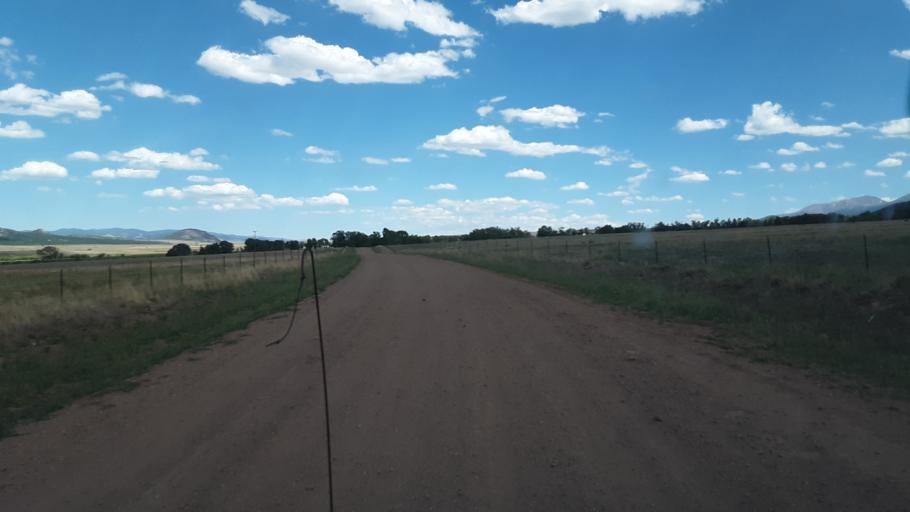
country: US
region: Colorado
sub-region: Custer County
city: Westcliffe
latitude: 38.2447
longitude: -105.6081
